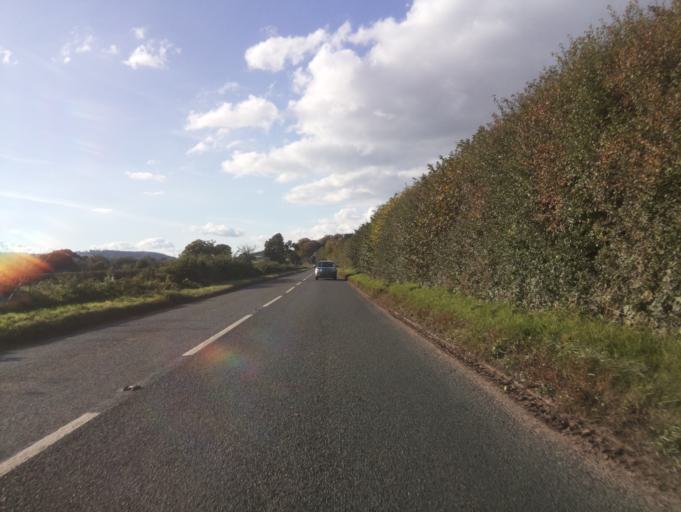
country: GB
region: England
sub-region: Herefordshire
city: Moccas
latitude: 52.0969
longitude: -2.9209
